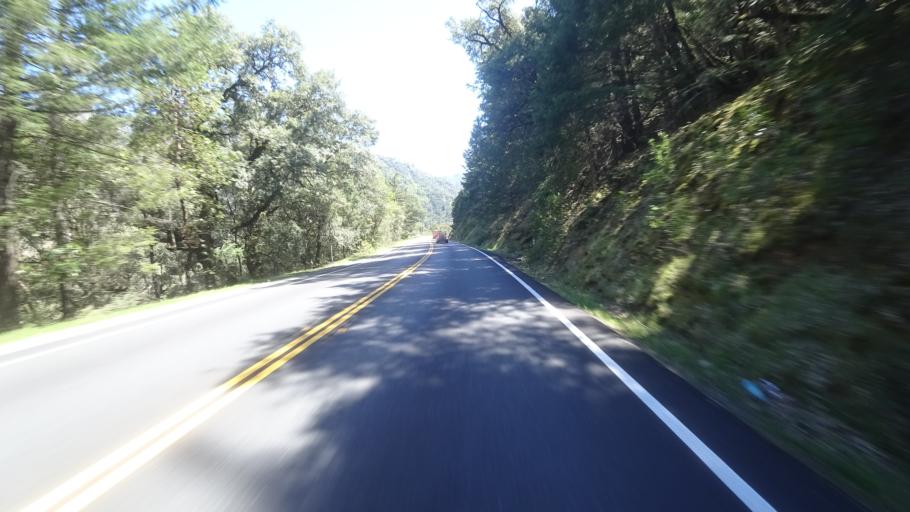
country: US
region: California
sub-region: Humboldt County
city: Willow Creek
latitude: 40.8048
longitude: -123.4683
